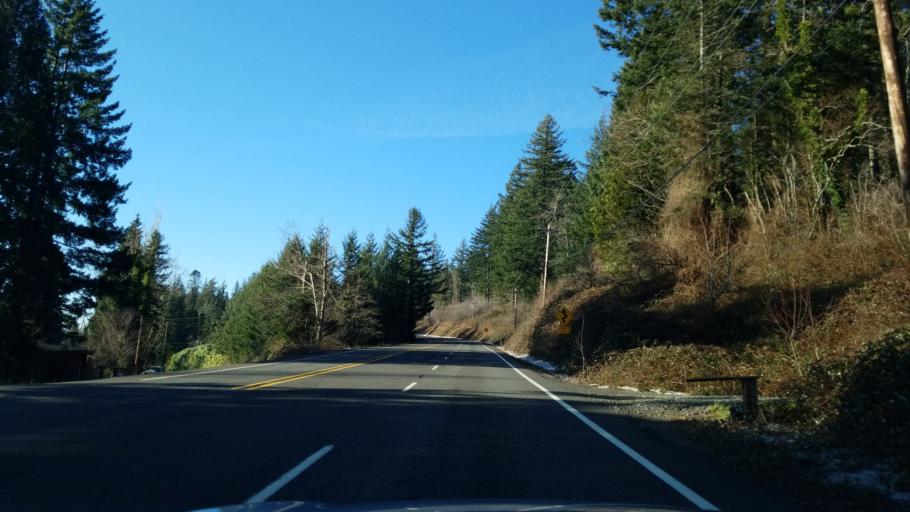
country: US
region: Washington
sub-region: Clark County
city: Washougal
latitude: 45.5917
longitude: -122.1522
